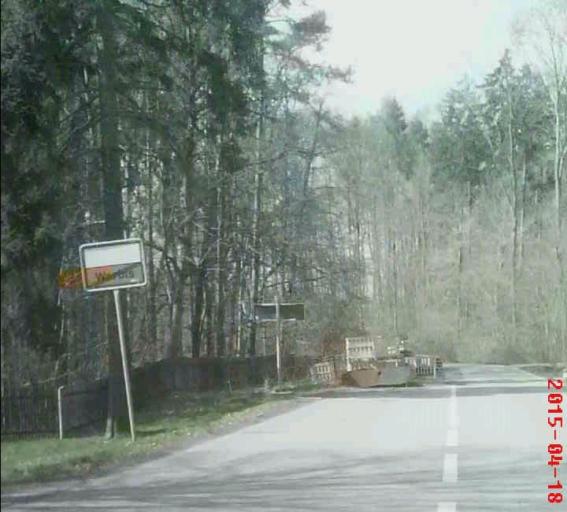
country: DE
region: Thuringia
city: Worbis
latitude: 51.4282
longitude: 10.3480
